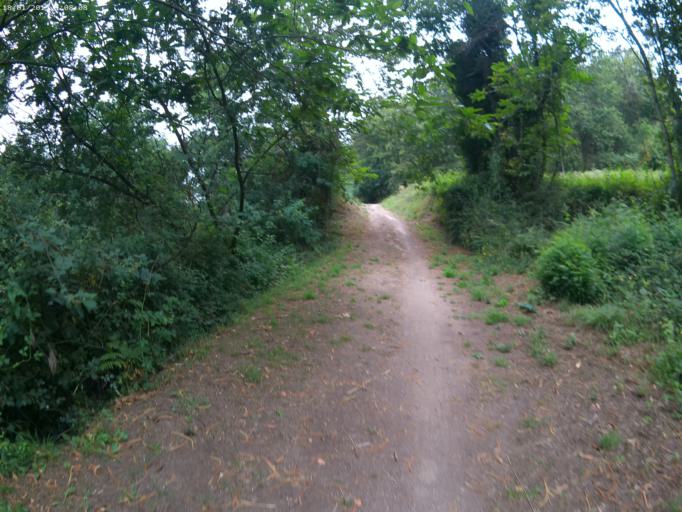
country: PT
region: Viana do Castelo
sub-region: Ponte da Barca
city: Ponte da Barca
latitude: 41.8069
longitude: -8.4479
